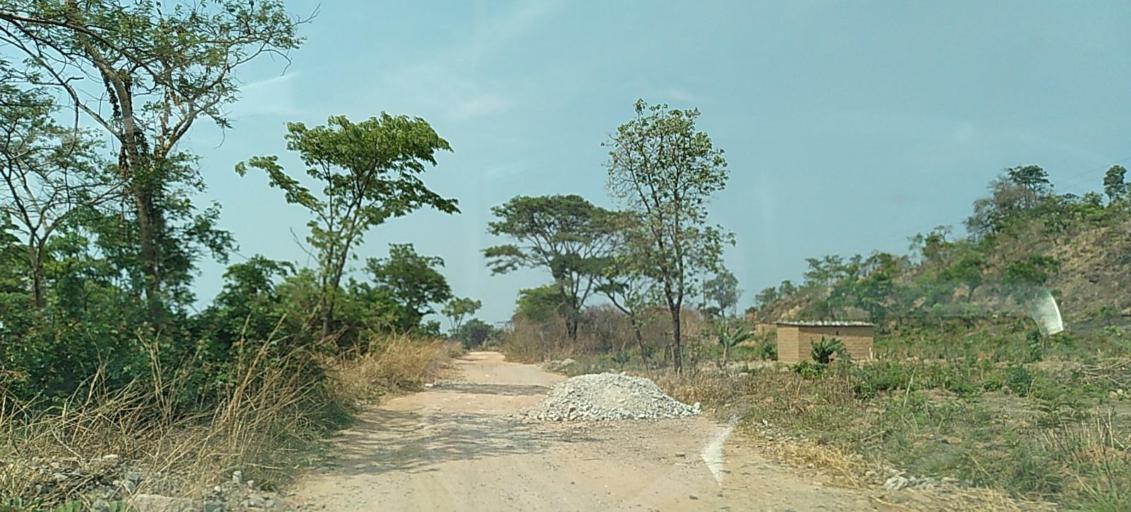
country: ZM
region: Copperbelt
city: Chililabombwe
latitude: -12.3319
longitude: 27.7303
